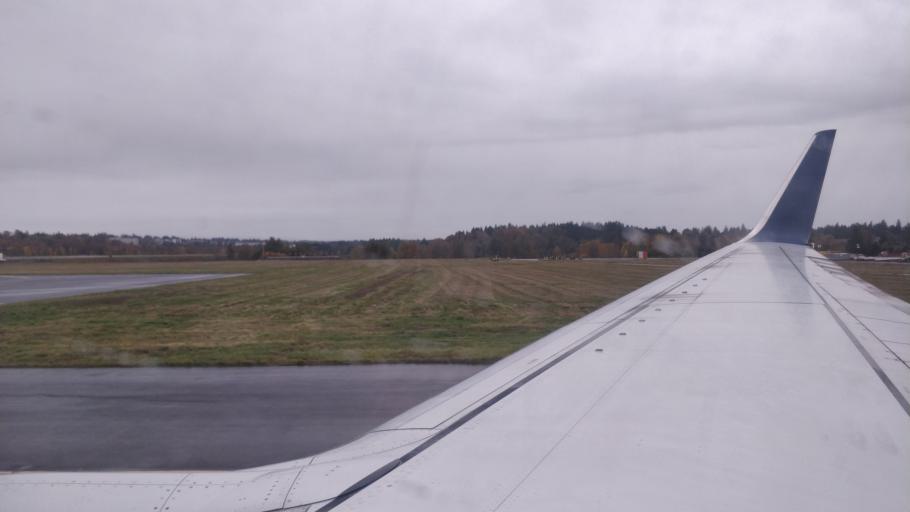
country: US
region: Washington
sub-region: King County
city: SeaTac
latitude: 47.4381
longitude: -122.3121
